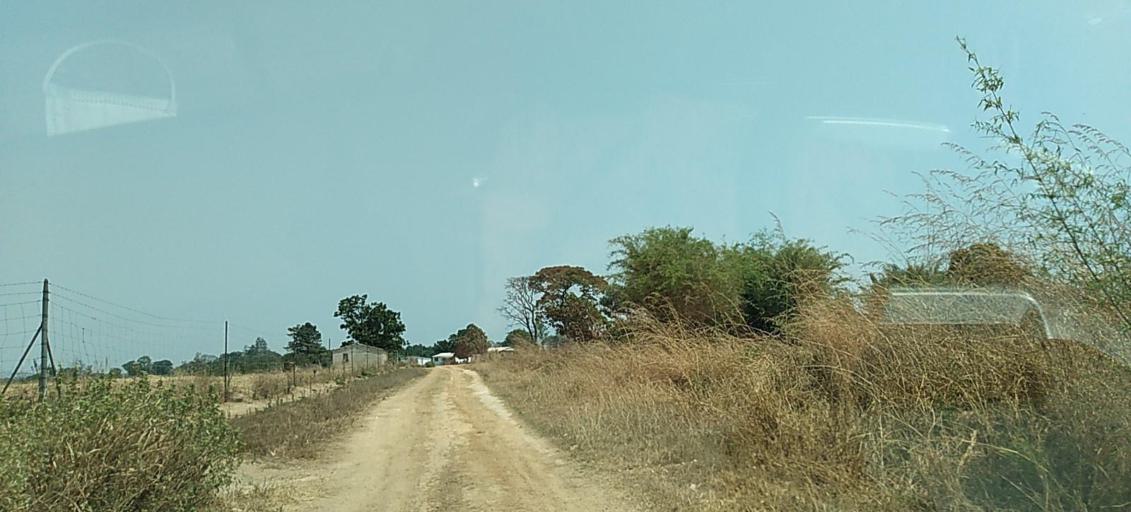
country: ZM
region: Copperbelt
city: Chambishi
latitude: -12.6279
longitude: 27.9409
